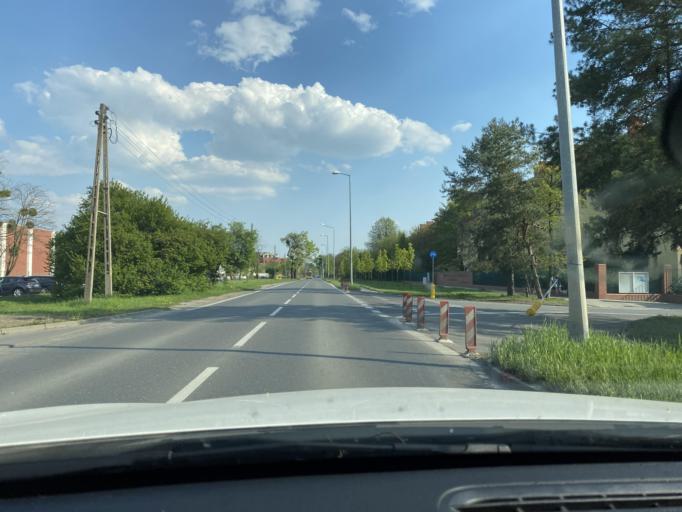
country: PL
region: Lower Silesian Voivodeship
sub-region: Powiat trzebnicki
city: Psary
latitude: 51.1466
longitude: 17.0217
